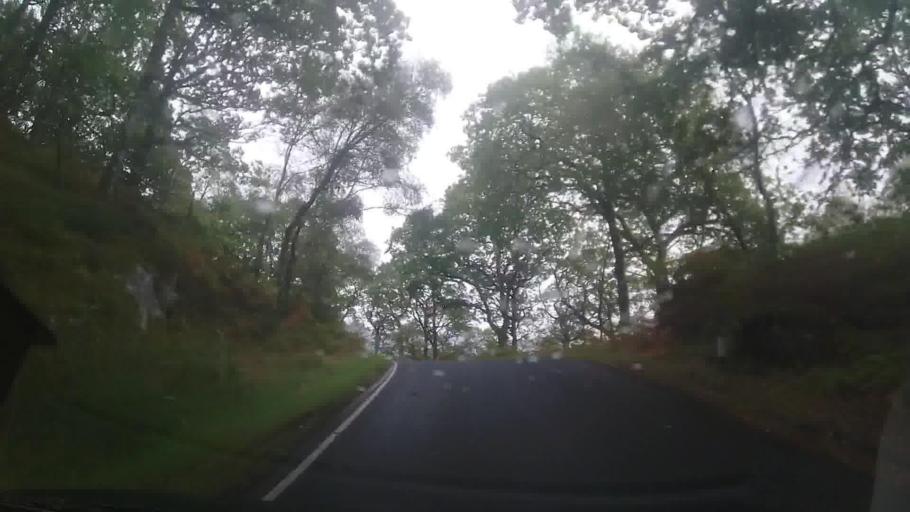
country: GB
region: Scotland
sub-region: Argyll and Bute
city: Isle Of Mull
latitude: 56.7000
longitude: -5.6971
